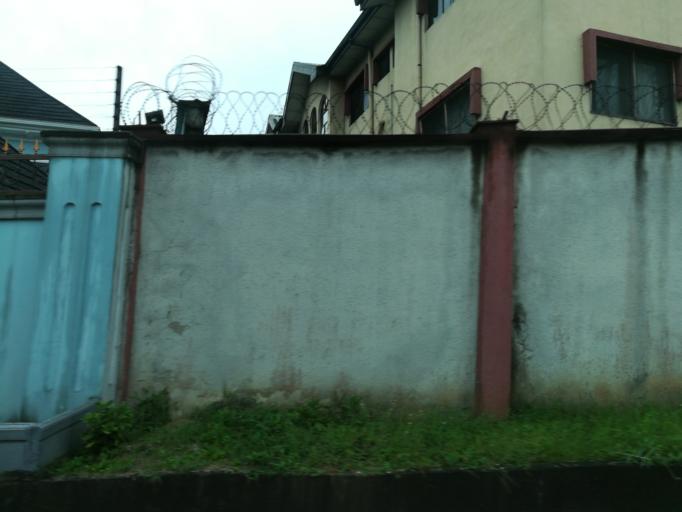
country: NG
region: Rivers
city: Port Harcourt
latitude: 4.8428
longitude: 7.0324
